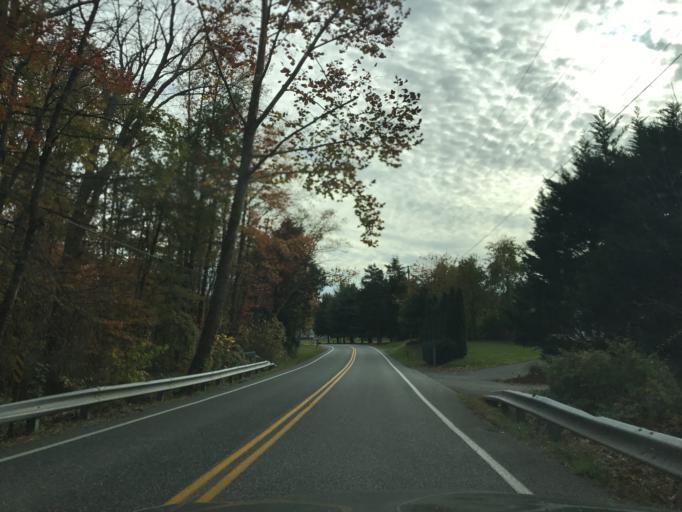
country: US
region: Maryland
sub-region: Harford County
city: Joppatowne
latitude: 39.4382
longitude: -76.3630
